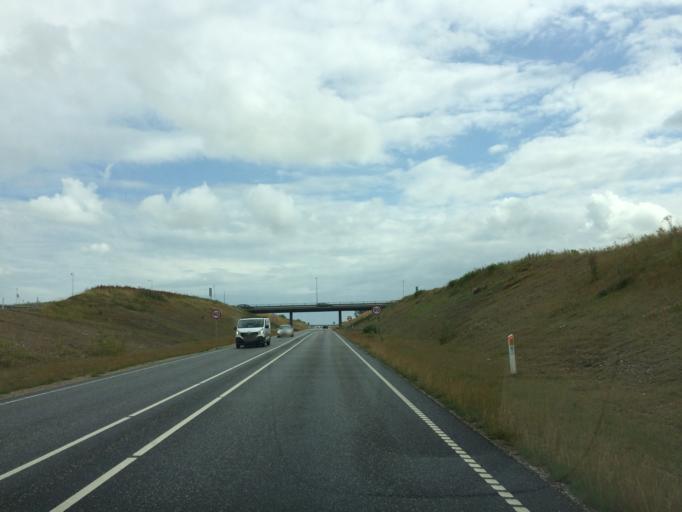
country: DK
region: Zealand
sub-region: Odsherred Kommune
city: Hojby
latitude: 55.8701
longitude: 11.5857
